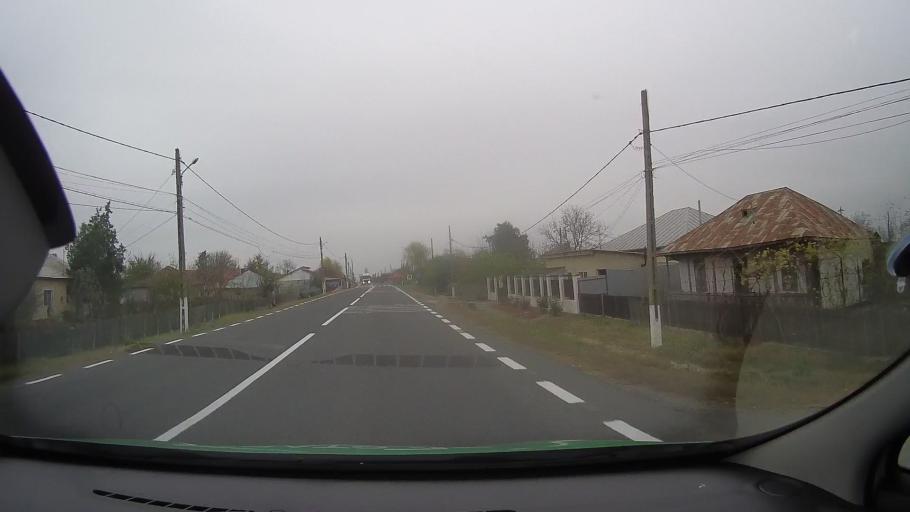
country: RO
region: Ialomita
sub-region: Comuna Giurgeni
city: Giurgeni
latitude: 44.7428
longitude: 27.8564
